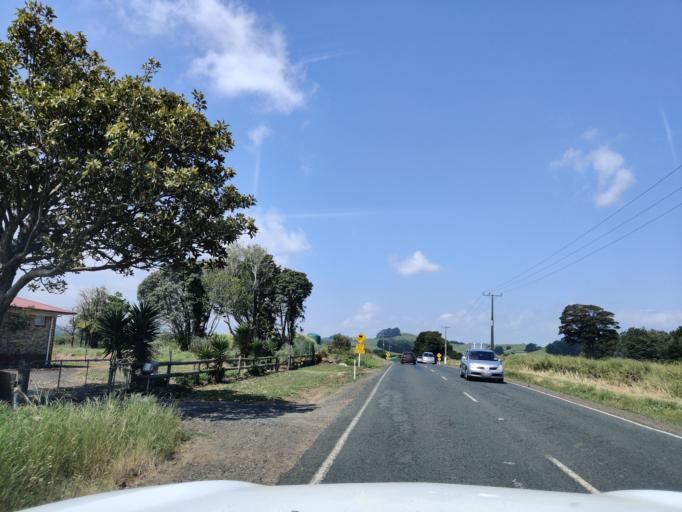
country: NZ
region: Auckland
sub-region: Auckland
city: Pukekohe East
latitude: -37.2392
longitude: 174.9554
